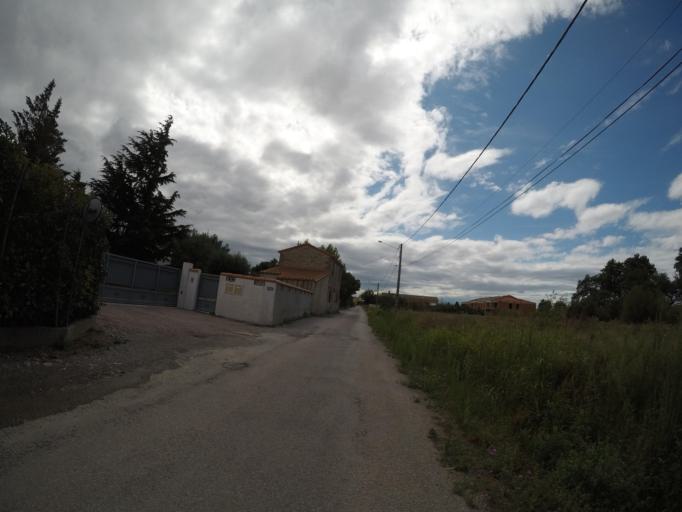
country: FR
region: Languedoc-Roussillon
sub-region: Departement des Pyrenees-Orientales
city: Pezilla-la-Riviere
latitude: 42.6998
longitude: 2.7798
